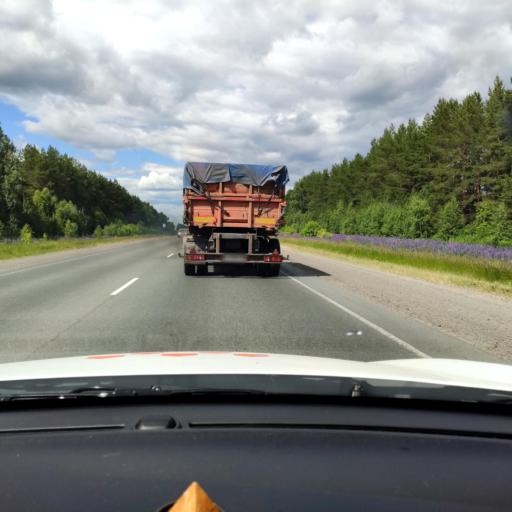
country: RU
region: Mariy-El
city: Pomary
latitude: 55.9485
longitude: 48.3685
